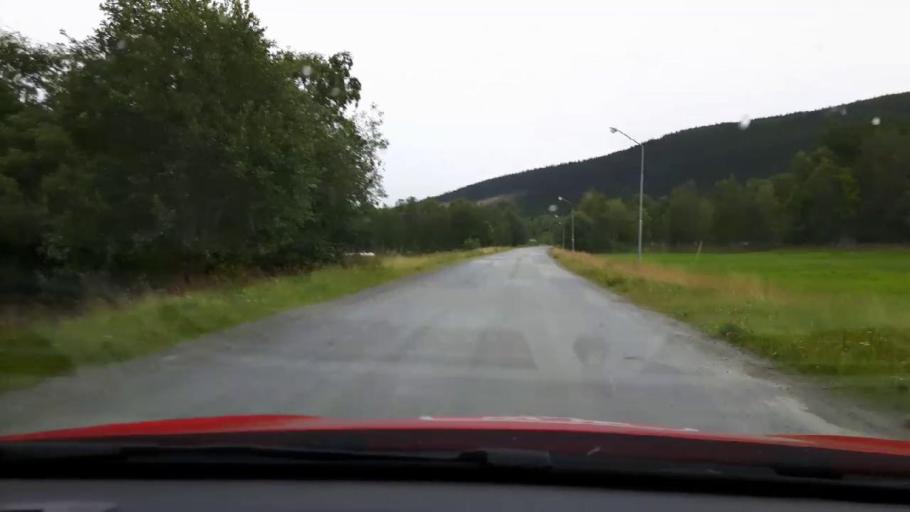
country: SE
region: Jaemtland
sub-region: Are Kommun
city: Are
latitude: 63.4932
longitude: 13.1245
